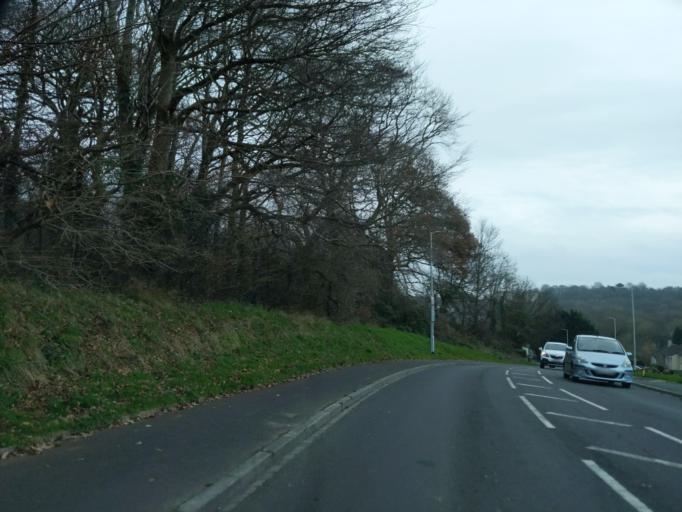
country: GB
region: England
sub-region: Plymouth
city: Plymouth
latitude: 50.4043
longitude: -4.1450
